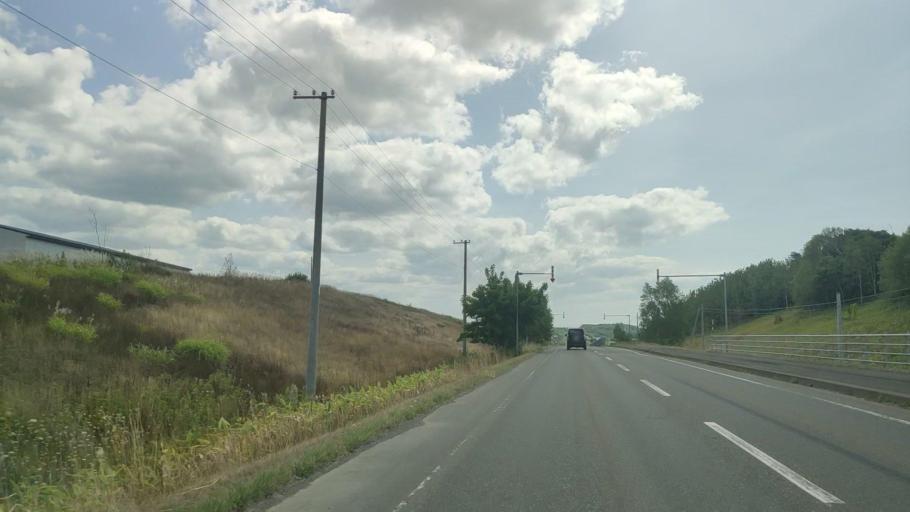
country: JP
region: Hokkaido
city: Makubetsu
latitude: 44.7805
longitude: 141.7909
